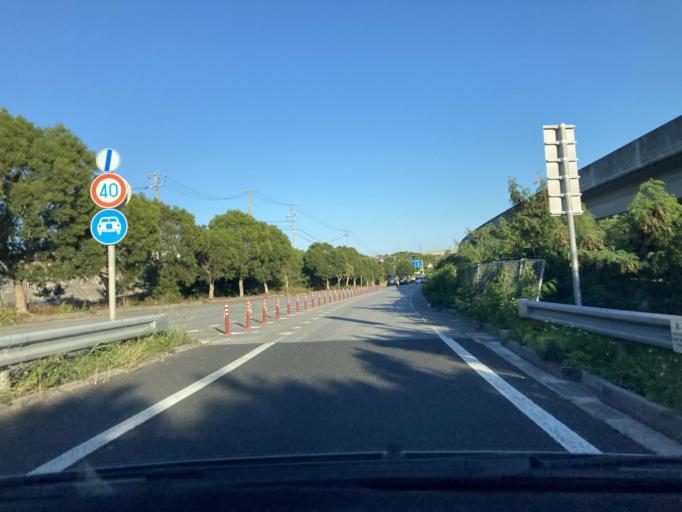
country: JP
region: Okinawa
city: Tomigusuku
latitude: 26.1814
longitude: 127.7215
